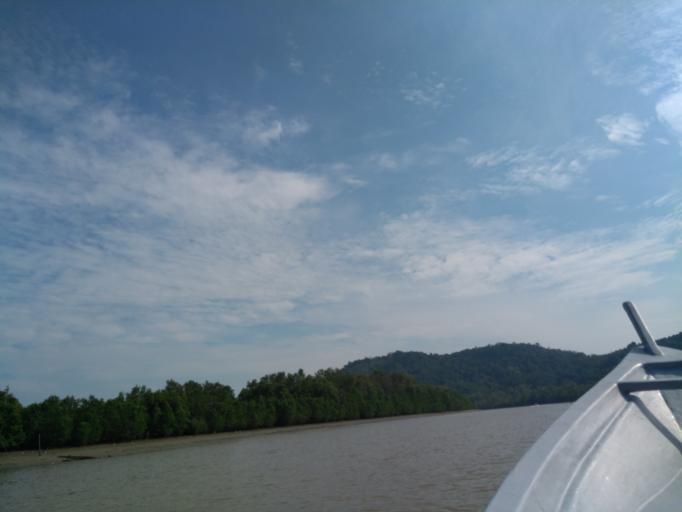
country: MY
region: Sarawak
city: Kuching
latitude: 1.6699
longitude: 110.4321
